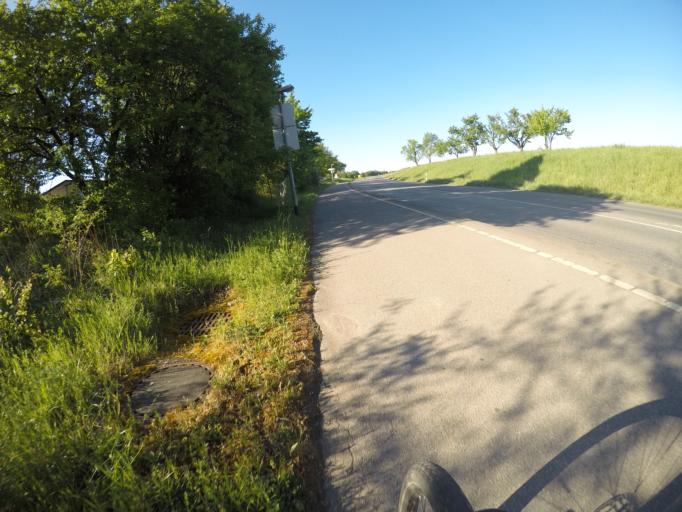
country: DE
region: Baden-Wuerttemberg
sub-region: Regierungsbezirk Stuttgart
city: Filderstadt
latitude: 48.6683
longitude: 9.2306
